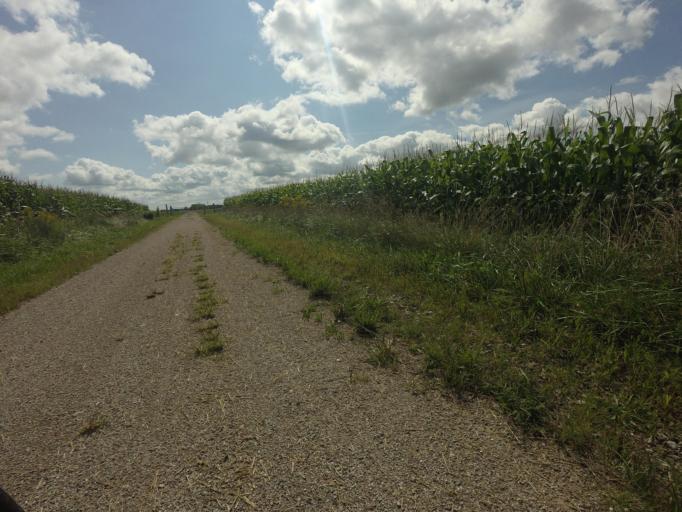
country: CA
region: Ontario
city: Huron East
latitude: 43.6441
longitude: -81.2124
